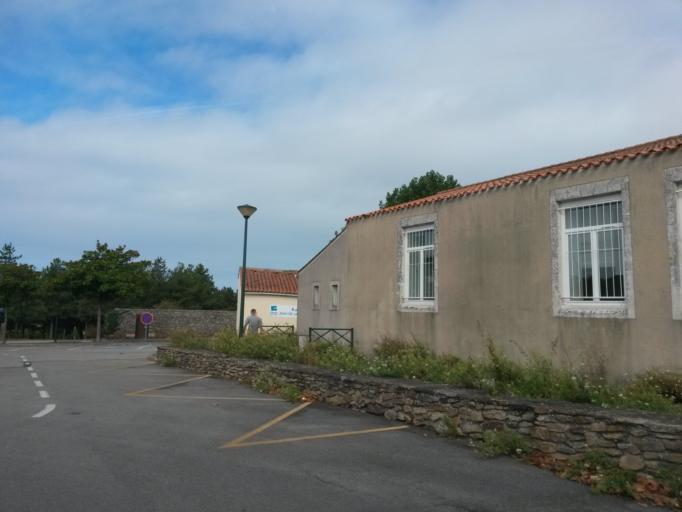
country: FR
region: Pays de la Loire
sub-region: Departement de la Vendee
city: Olonne-sur-Mer
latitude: 46.5358
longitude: -1.7747
